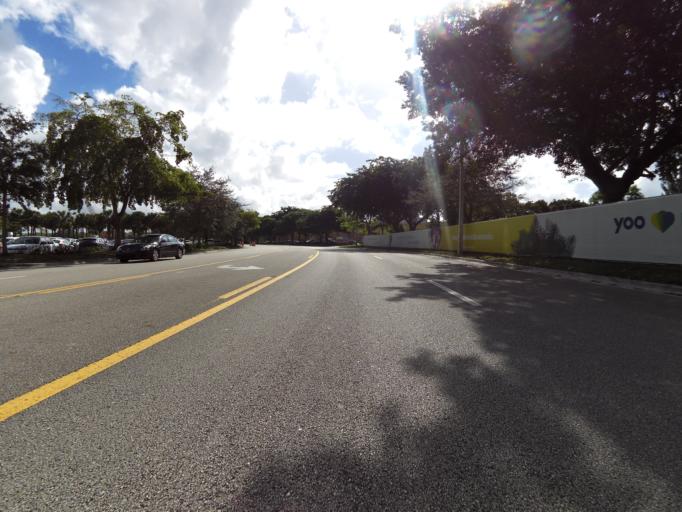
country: US
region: Florida
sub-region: Broward County
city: Pine Island Ridge
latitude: 26.1485
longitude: -80.3269
